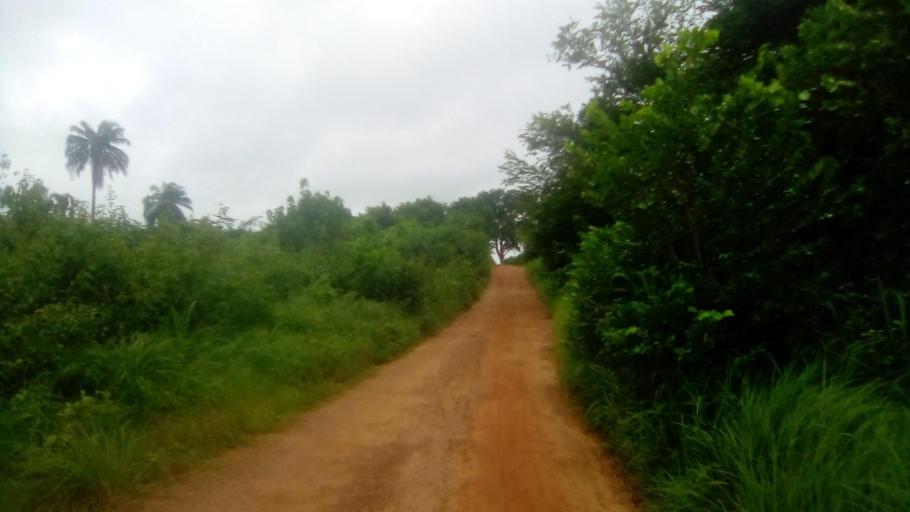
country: SL
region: Eastern Province
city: Kailahun
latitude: 8.2998
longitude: -10.5577
